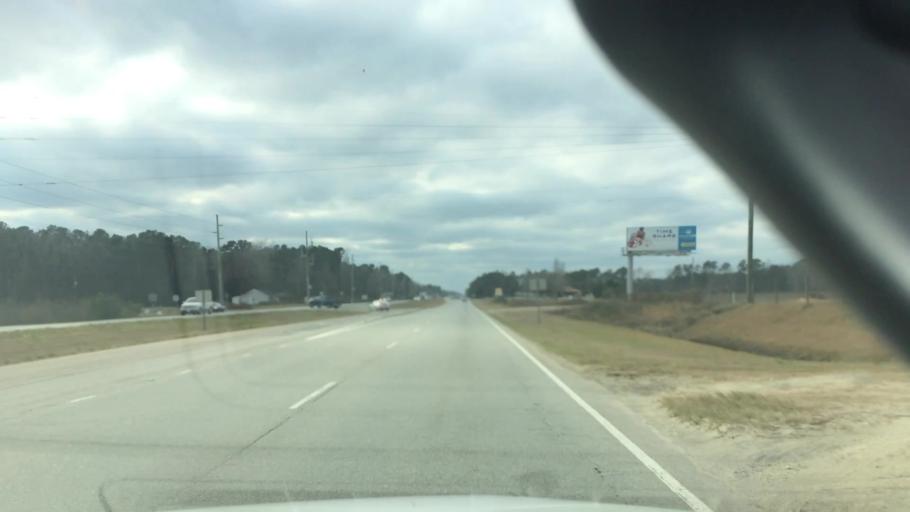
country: US
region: North Carolina
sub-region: Brunswick County
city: Shallotte
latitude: 33.9550
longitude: -78.4469
